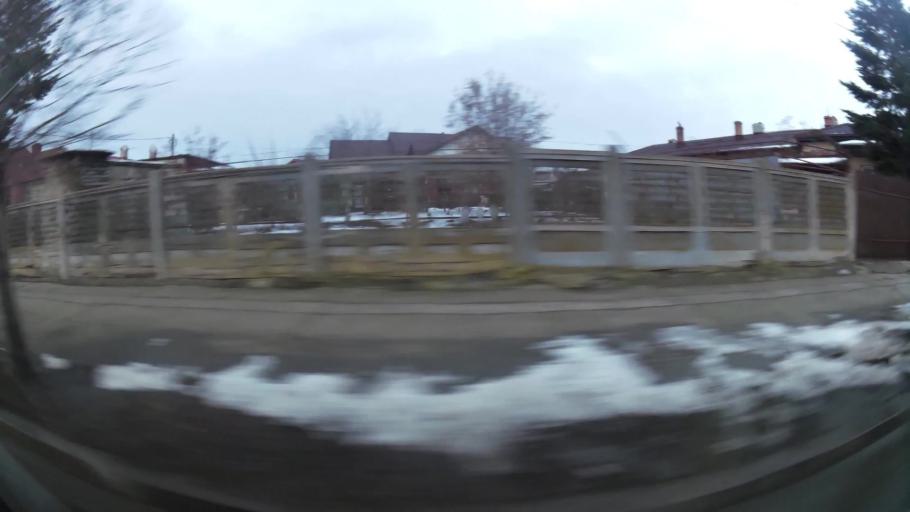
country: RO
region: Ilfov
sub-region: Comuna Popesti-Leordeni
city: Popesti-Leordeni
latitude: 44.3818
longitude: 26.1735
